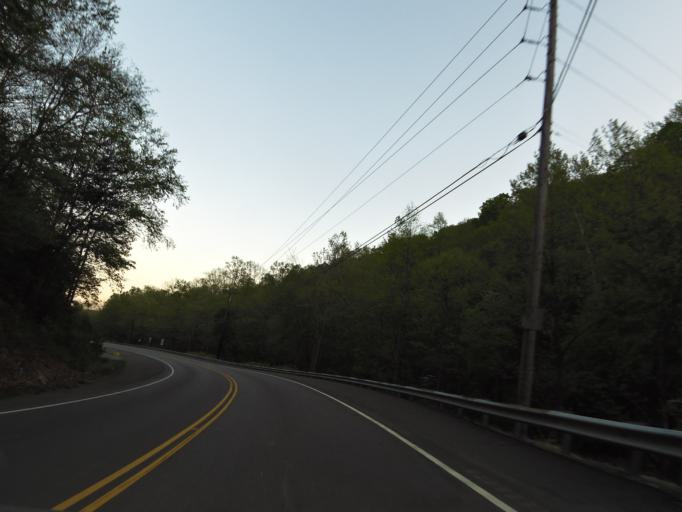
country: US
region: Tennessee
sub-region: Campbell County
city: LaFollette
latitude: 36.3907
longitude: -84.1274
